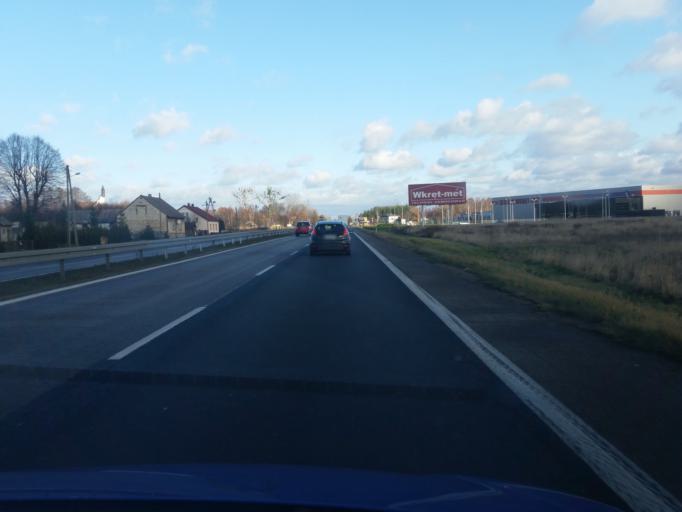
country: PL
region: Silesian Voivodeship
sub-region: Powiat czestochowski
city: Kamienica Polska
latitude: 50.6840
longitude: 19.1307
